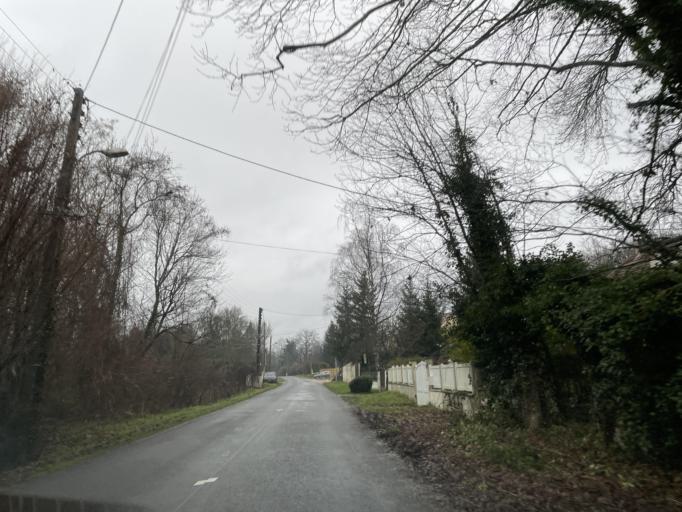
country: FR
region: Ile-de-France
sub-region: Departement de Seine-et-Marne
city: Pommeuse
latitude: 48.8063
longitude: 3.0210
